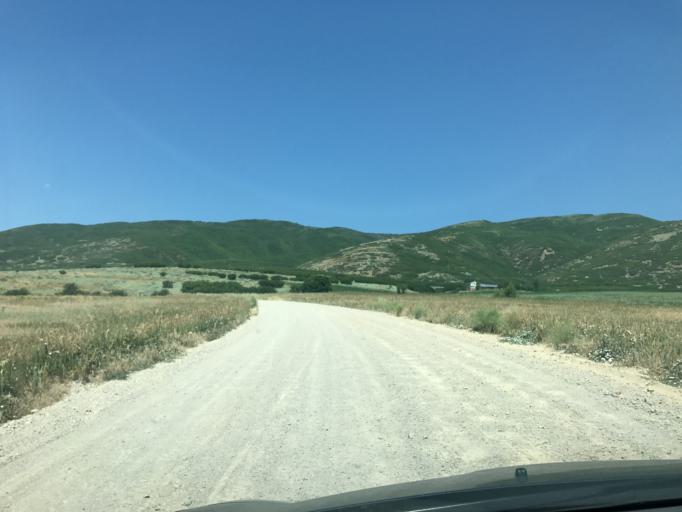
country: US
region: Utah
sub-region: Wasatch County
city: Midway
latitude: 40.4921
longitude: -111.4935
